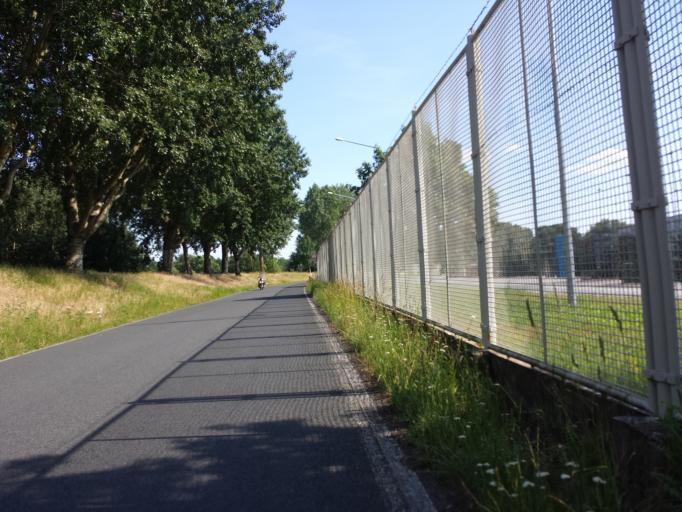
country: DE
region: Bremen
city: Bremen
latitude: 53.1013
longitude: 8.7480
